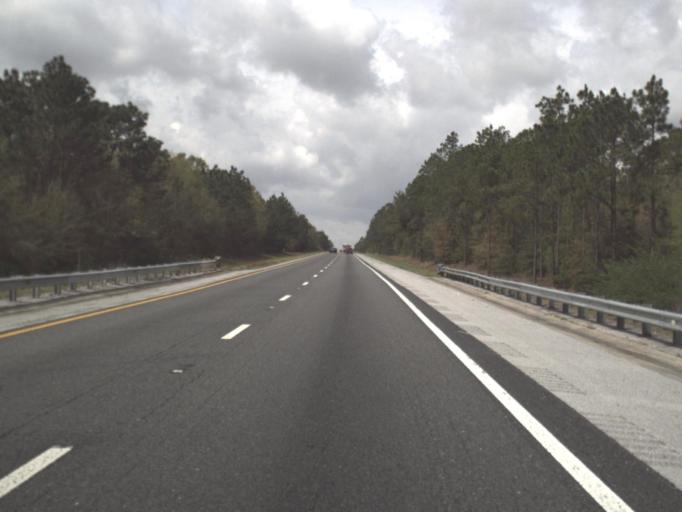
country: US
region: Florida
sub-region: Okaloosa County
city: Crestview
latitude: 30.7140
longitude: -86.6965
